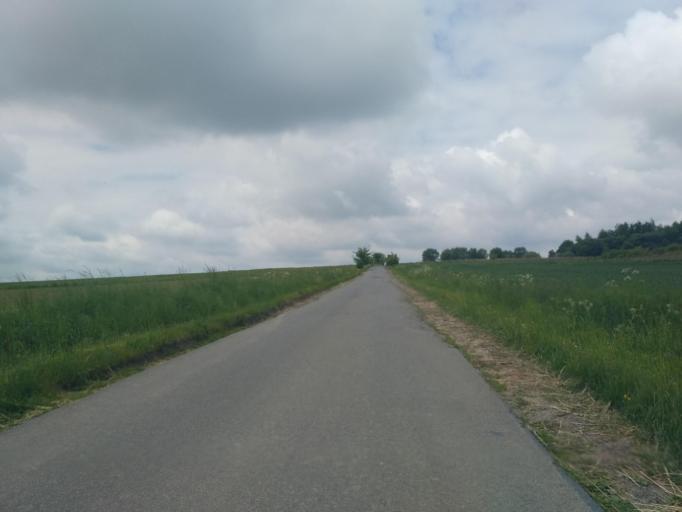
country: PL
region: Subcarpathian Voivodeship
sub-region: Powiat krosnienski
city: Chorkowka
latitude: 49.6714
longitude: 21.6488
